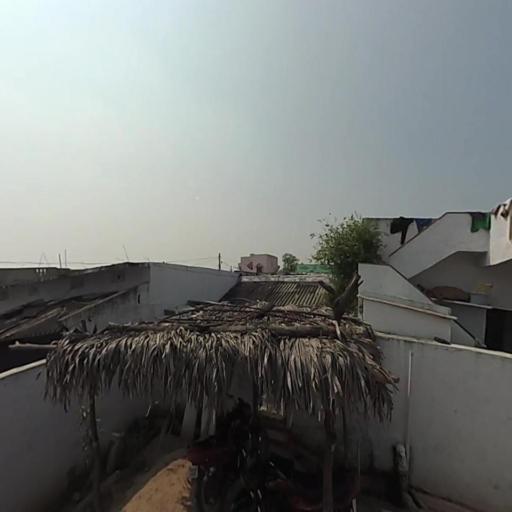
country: IN
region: Telangana
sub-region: Nalgonda
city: Nalgonda
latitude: 17.2099
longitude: 79.1573
